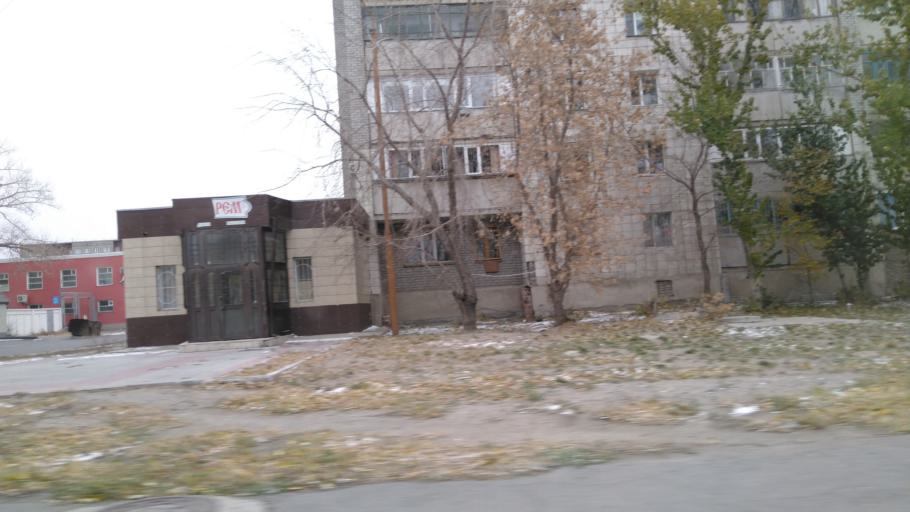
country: KZ
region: Pavlodar
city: Pavlodar
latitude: 52.2773
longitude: 76.9621
